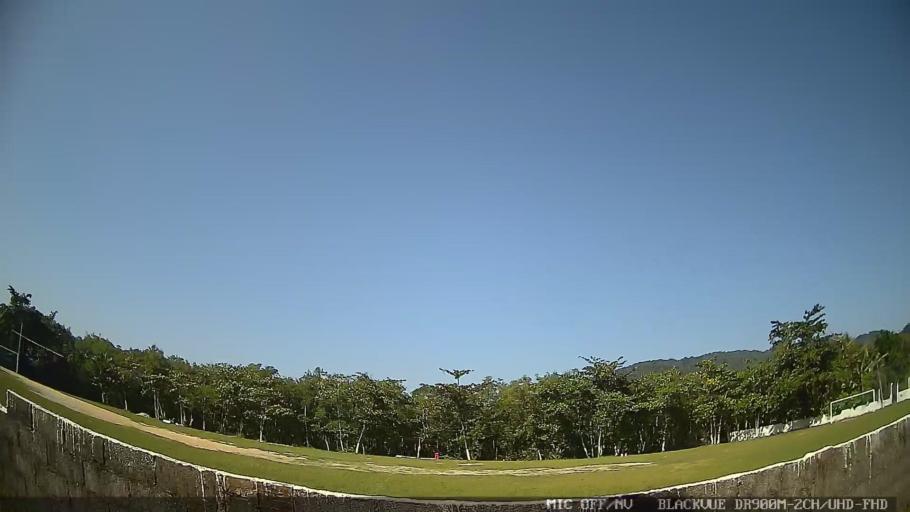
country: BR
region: Sao Paulo
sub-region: Santos
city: Santos
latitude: -23.9965
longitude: -46.3081
